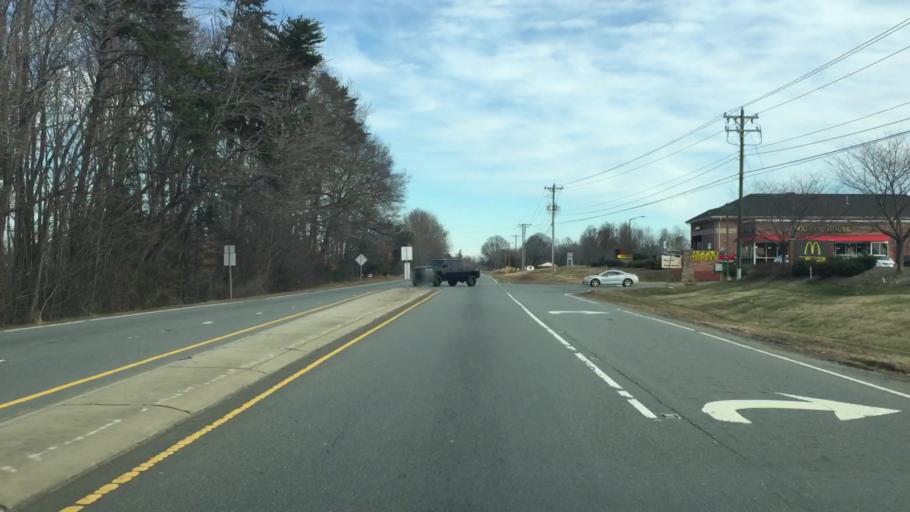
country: US
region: North Carolina
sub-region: Forsyth County
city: Walkertown
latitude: 36.1665
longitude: -80.1355
